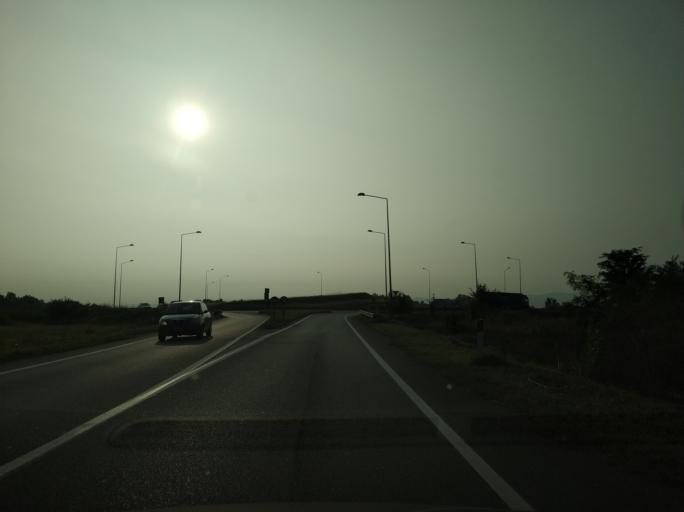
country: IT
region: Piedmont
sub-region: Provincia di Torino
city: Venaria Reale
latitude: 45.1520
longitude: 7.6214
